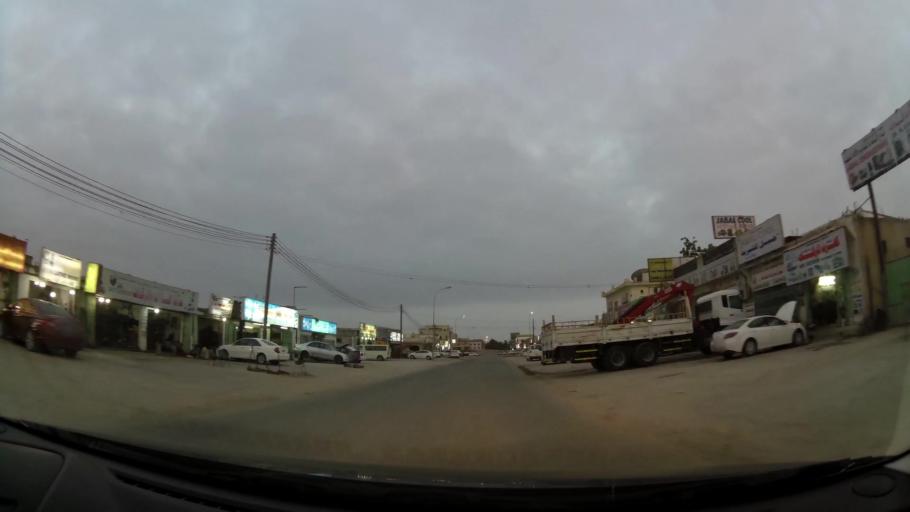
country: OM
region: Zufar
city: Salalah
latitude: 17.0184
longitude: 54.0529
